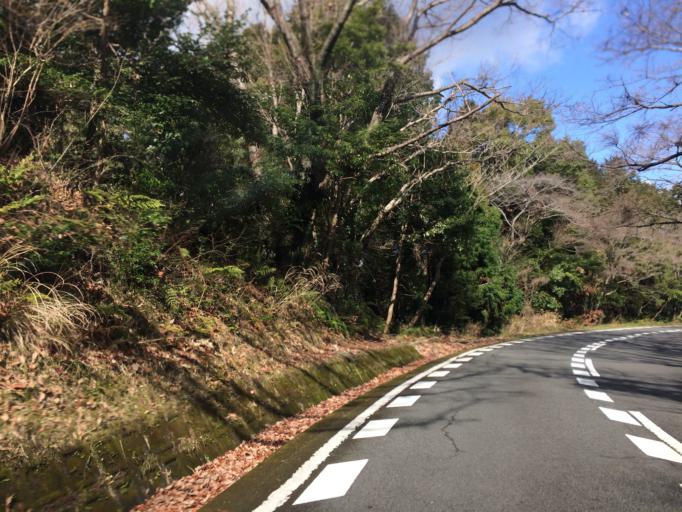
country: JP
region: Shizuoka
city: Shizuoka-shi
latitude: 34.9731
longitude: 138.4481
